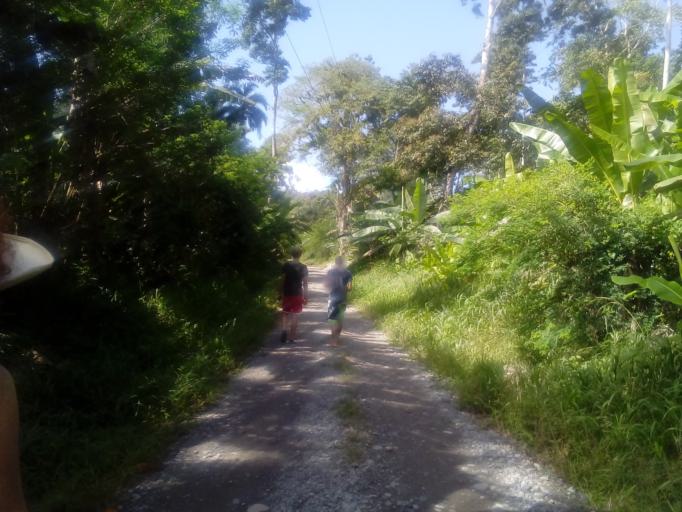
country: PA
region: Bocas del Toro
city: Barranco
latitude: 9.5082
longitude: -82.9855
